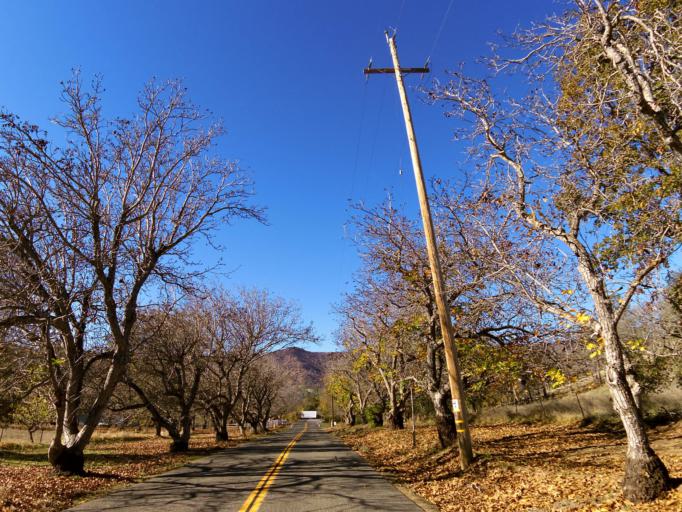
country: US
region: California
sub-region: Yolo County
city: Winters
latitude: 38.4699
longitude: -122.0372
